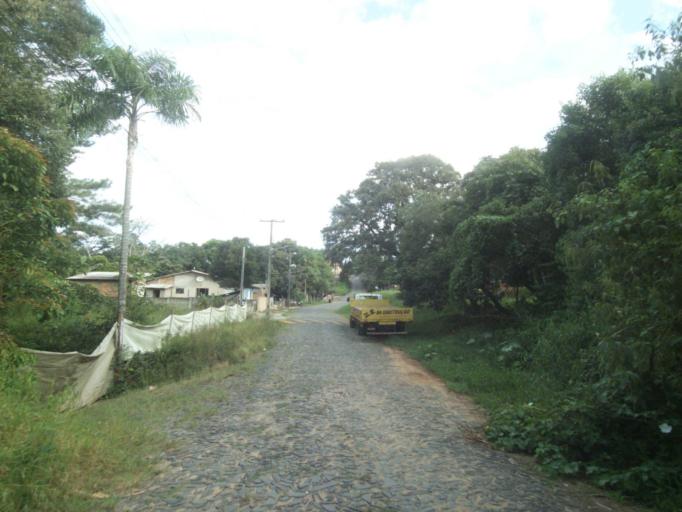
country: BR
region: Parana
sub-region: Telemaco Borba
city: Telemaco Borba
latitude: -24.3248
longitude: -50.6082
